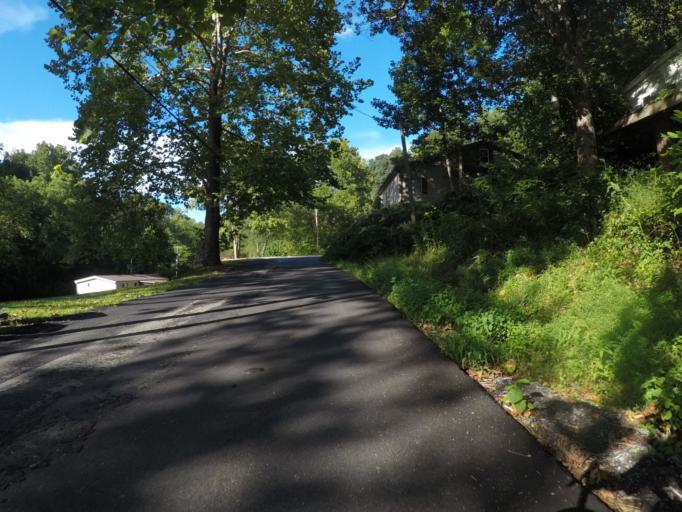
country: US
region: West Virginia
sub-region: Cabell County
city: Huntington
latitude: 38.4520
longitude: -82.4676
